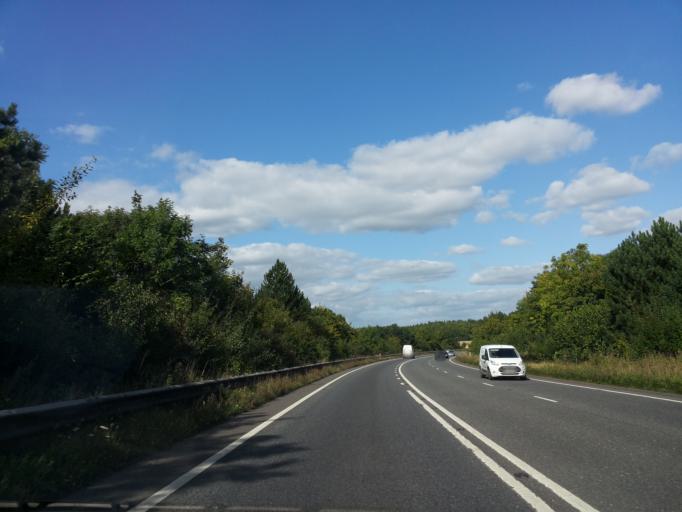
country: GB
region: England
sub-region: Wiltshire
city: Corsley
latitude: 51.2014
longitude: -2.2169
